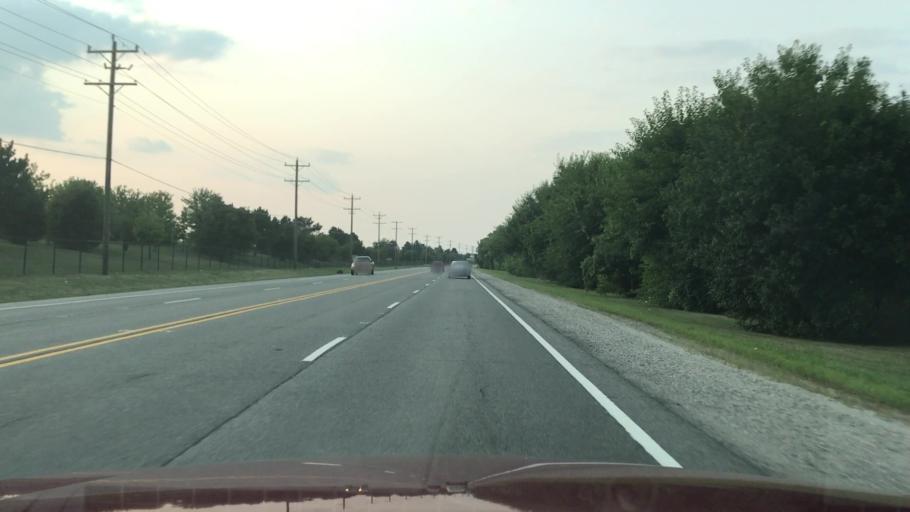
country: US
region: Illinois
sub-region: Will County
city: Lockport
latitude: 41.6156
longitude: -88.0769
